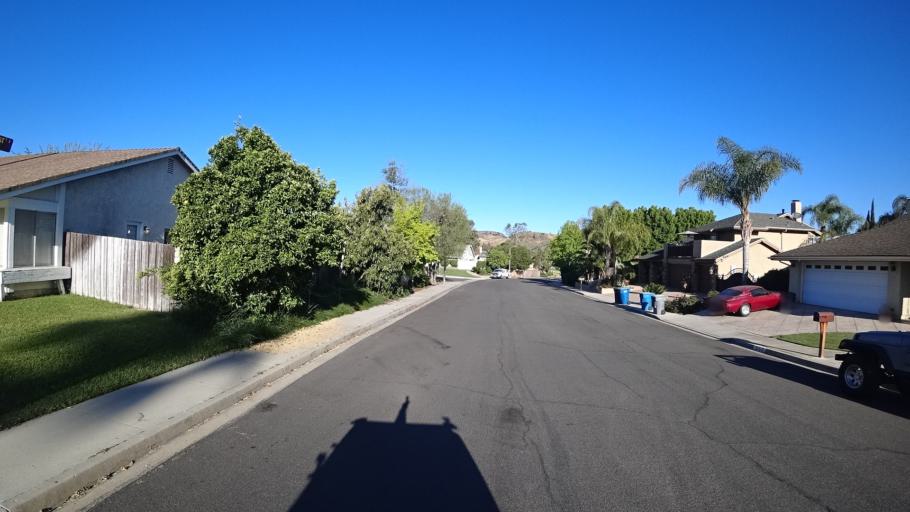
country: US
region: California
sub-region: Ventura County
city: Casa Conejo
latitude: 34.2188
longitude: -118.8914
